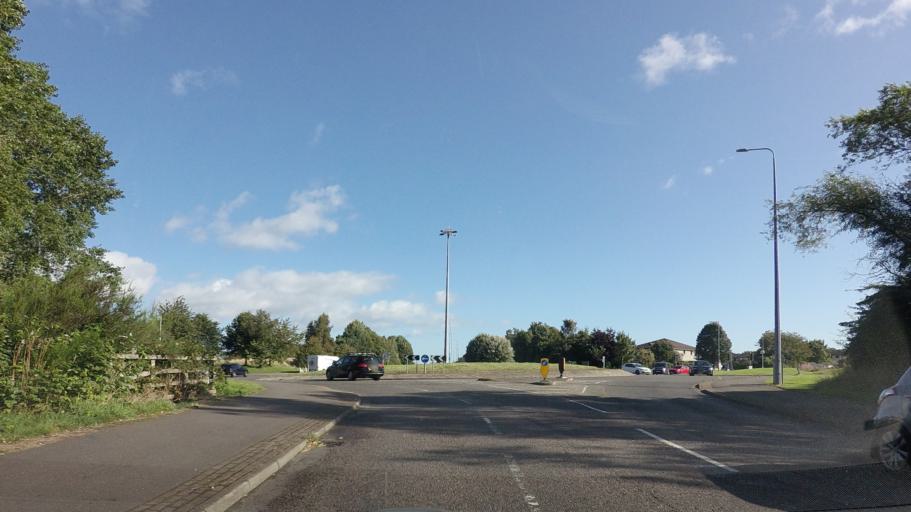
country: GB
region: Scotland
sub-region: Highland
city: Inverness
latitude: 57.4588
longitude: -4.2011
